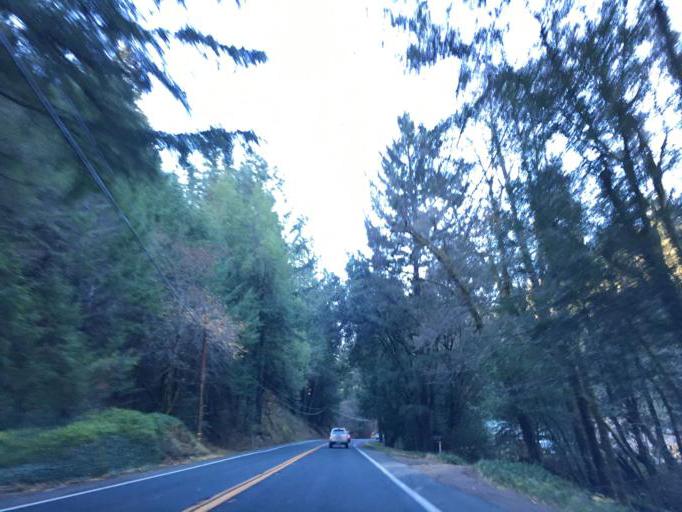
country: US
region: California
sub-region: Mendocino County
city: Brooktrails
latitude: 39.5088
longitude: -123.3838
